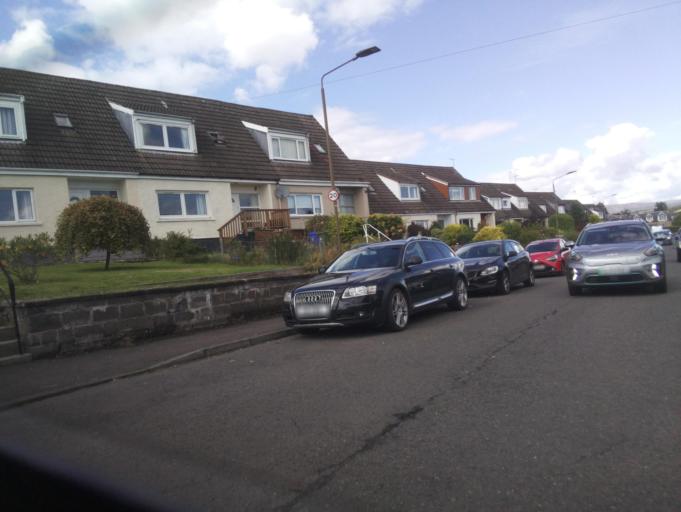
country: GB
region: Scotland
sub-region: Stirling
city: Dunblane
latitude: 56.1844
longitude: -3.9716
